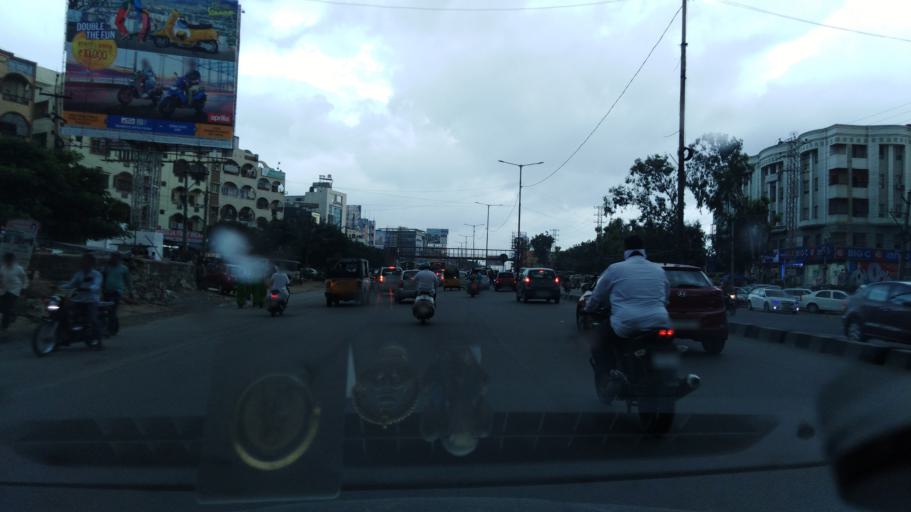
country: IN
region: Telangana
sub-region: Rangareddi
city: Kukatpalli
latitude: 17.4961
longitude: 78.3587
